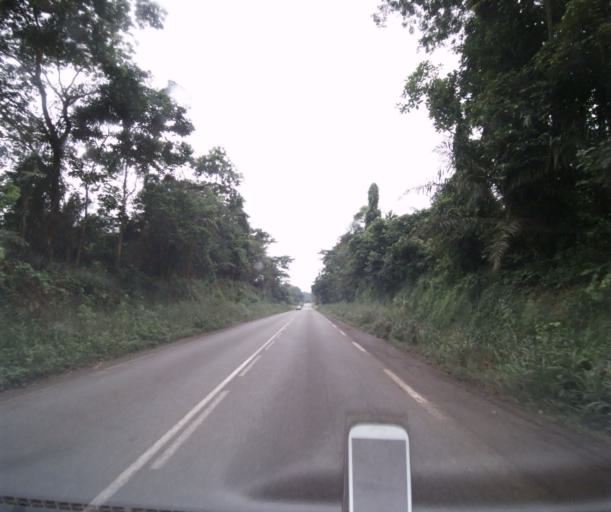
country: CM
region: Littoral
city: Edea
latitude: 3.8078
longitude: 10.2821
